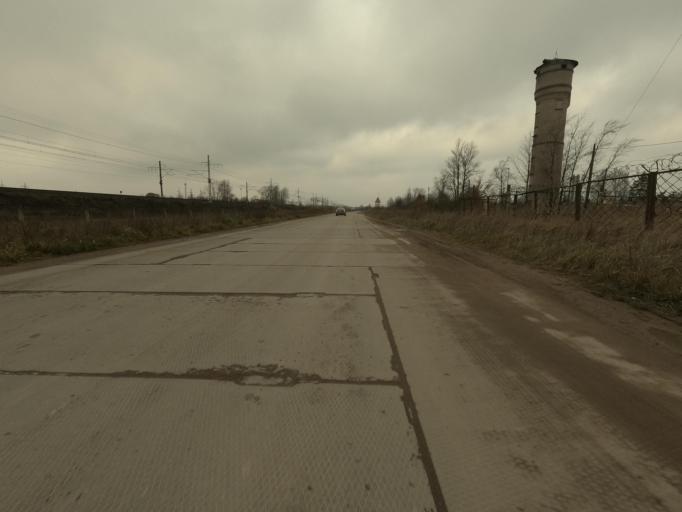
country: RU
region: Leningrad
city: Lyuban'
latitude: 59.4715
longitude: 31.2541
